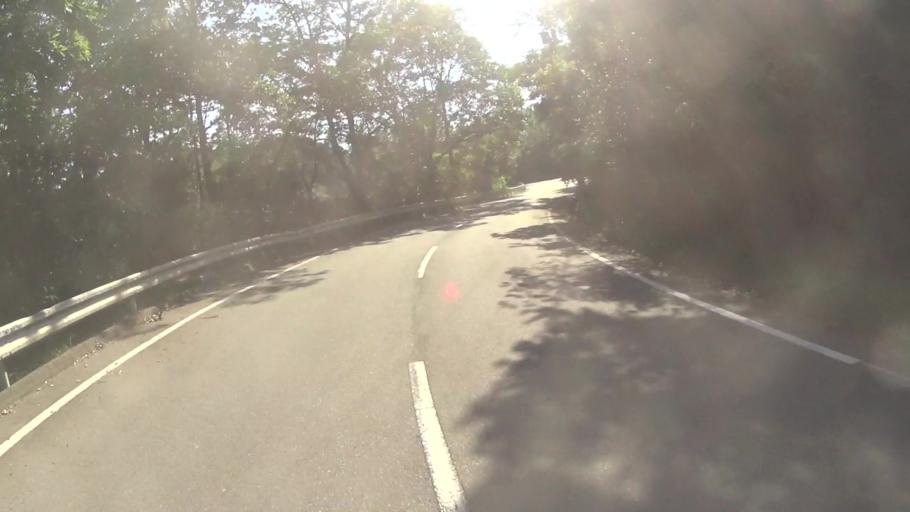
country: JP
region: Kyoto
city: Kameoka
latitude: 34.9220
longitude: 135.5589
